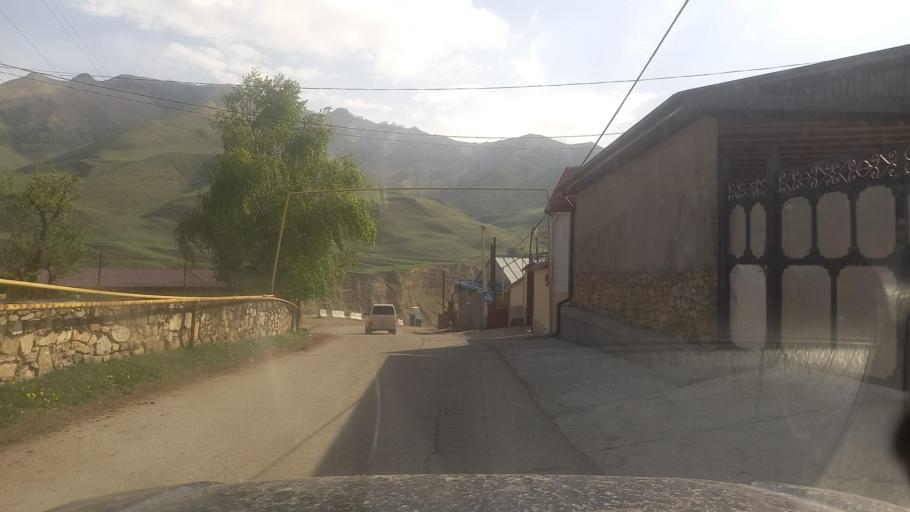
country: RU
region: Kabardino-Balkariya
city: Kamennomostskoye
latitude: 43.7266
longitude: 42.9234
